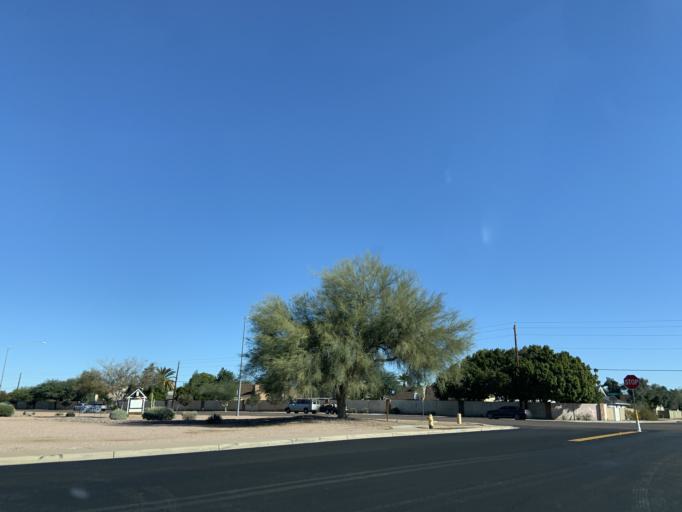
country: US
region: Arizona
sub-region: Maricopa County
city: San Carlos
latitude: 33.3681
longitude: -111.8598
